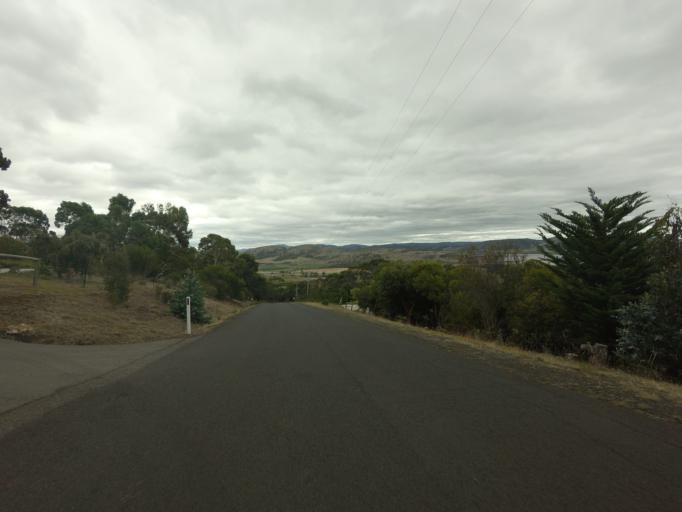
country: AU
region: Tasmania
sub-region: Clarence
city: Cambridge
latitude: -42.7894
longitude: 147.4093
